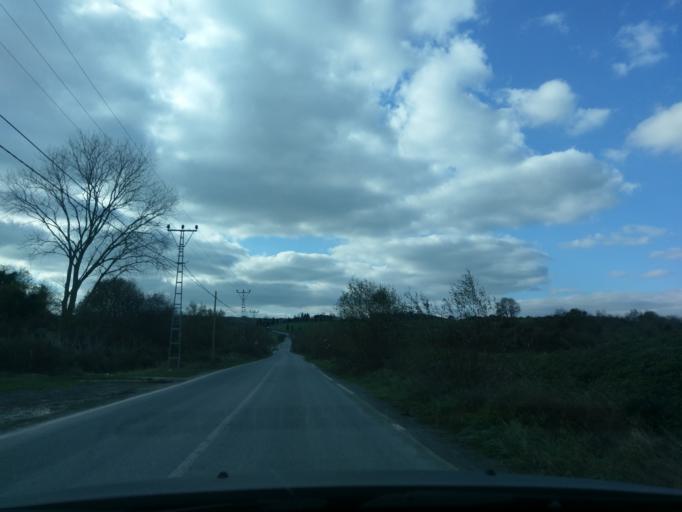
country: TR
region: Istanbul
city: Durusu
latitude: 41.3126
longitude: 28.6993
